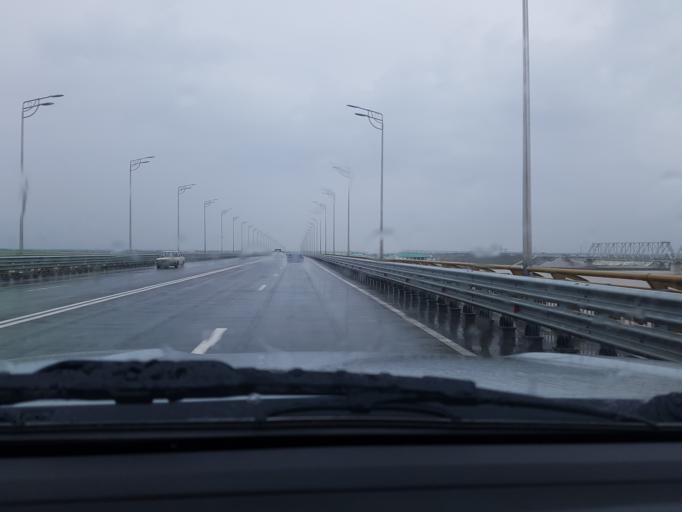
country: TM
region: Lebap
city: Turkmenabat
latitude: 39.1280
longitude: 63.5674
